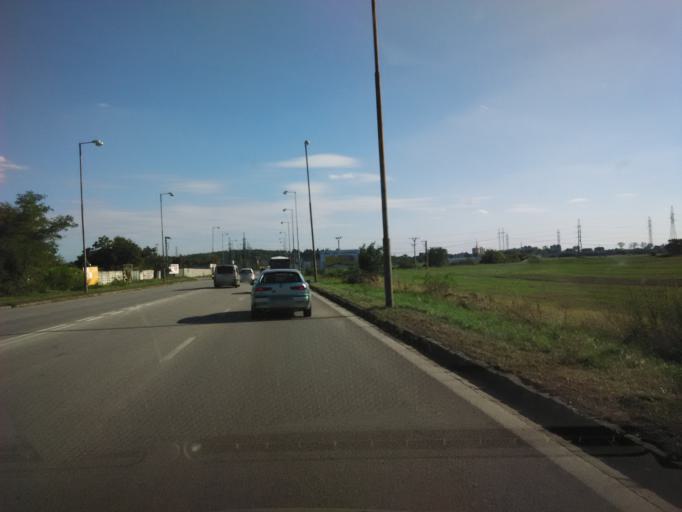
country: SK
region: Nitriansky
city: Levice
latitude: 48.2374
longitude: 18.5969
